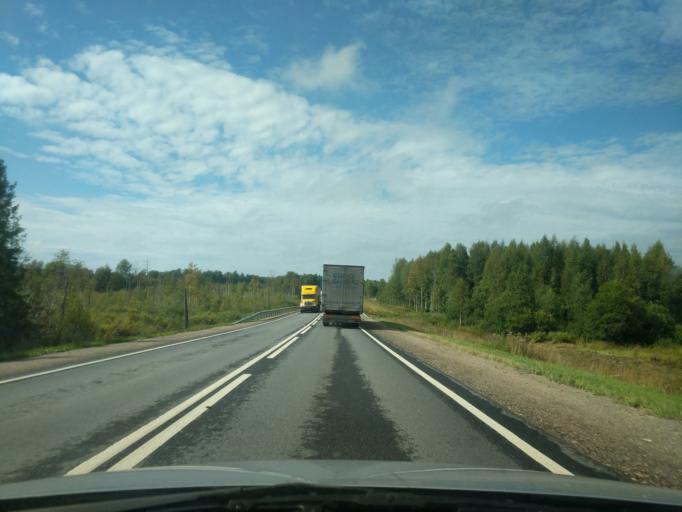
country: RU
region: Kostroma
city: Sudislavl'
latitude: 57.8432
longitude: 41.8331
